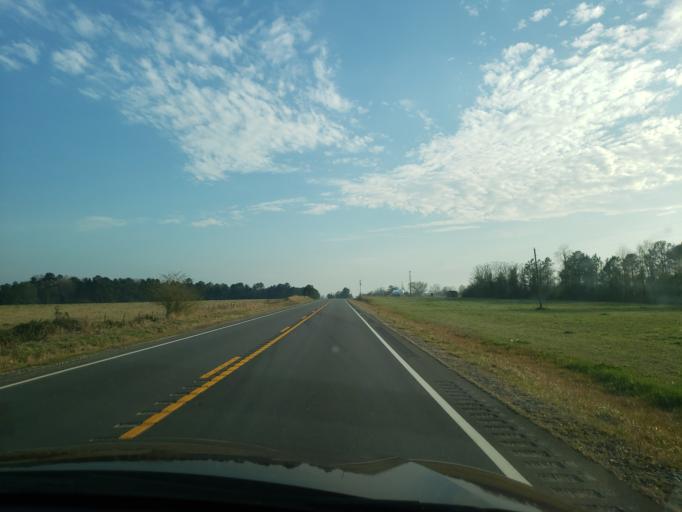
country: US
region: Alabama
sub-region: Hale County
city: Moundville
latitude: 32.8719
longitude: -87.6114
